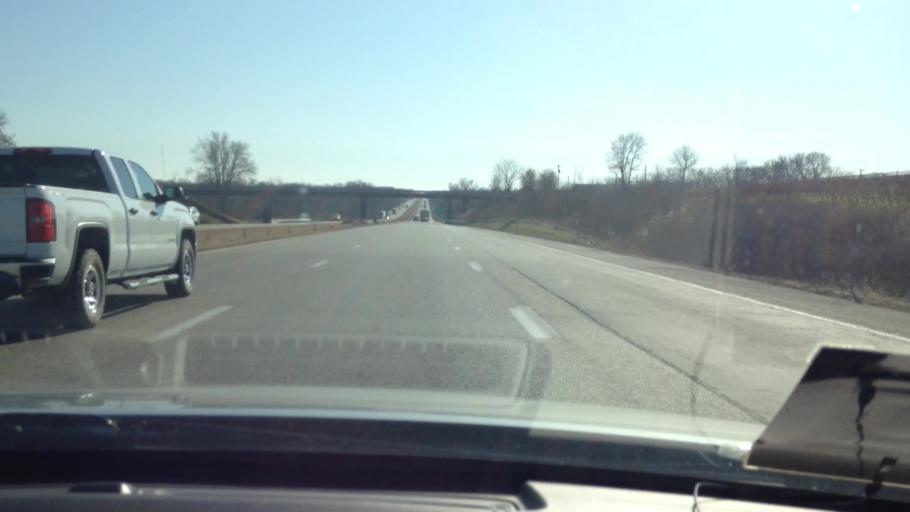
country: US
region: Missouri
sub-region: Platte County
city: Platte City
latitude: 39.4731
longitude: -94.7875
